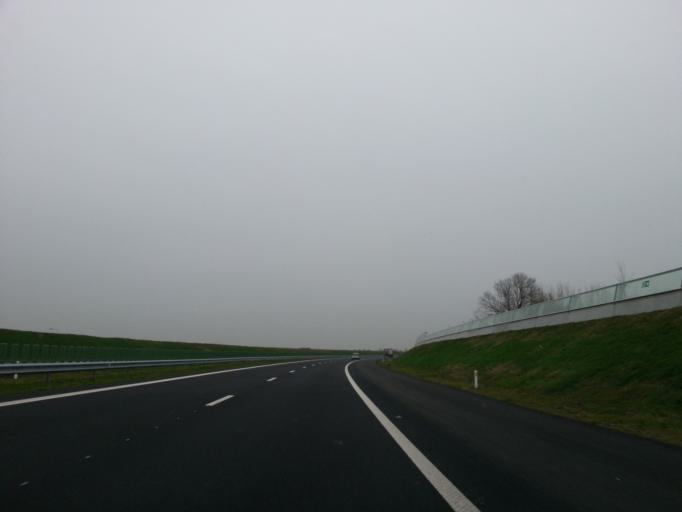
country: NL
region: North Brabant
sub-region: Gemeente Bergen op Zoom
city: Lepelstraat
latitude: 51.5610
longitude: 4.2891
